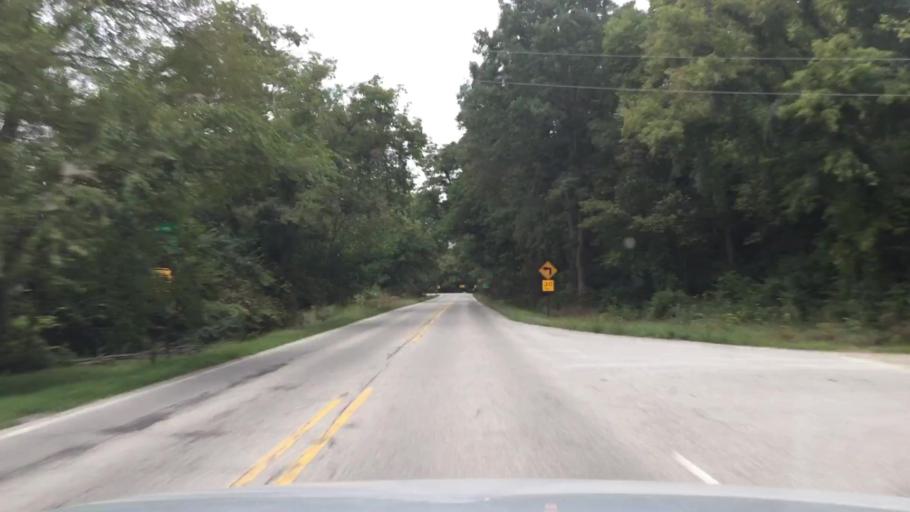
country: US
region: Michigan
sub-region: Washtenaw County
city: Milan
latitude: 42.1067
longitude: -83.7314
